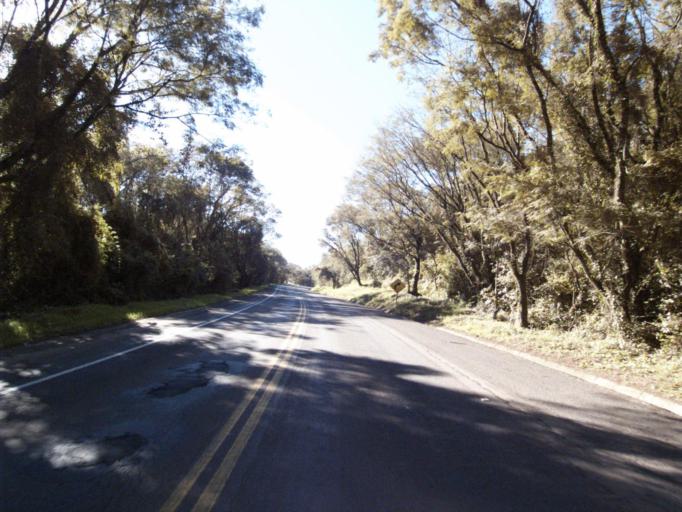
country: BR
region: Rio Grande do Sul
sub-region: Frederico Westphalen
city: Frederico Westphalen
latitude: -26.7931
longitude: -53.4541
